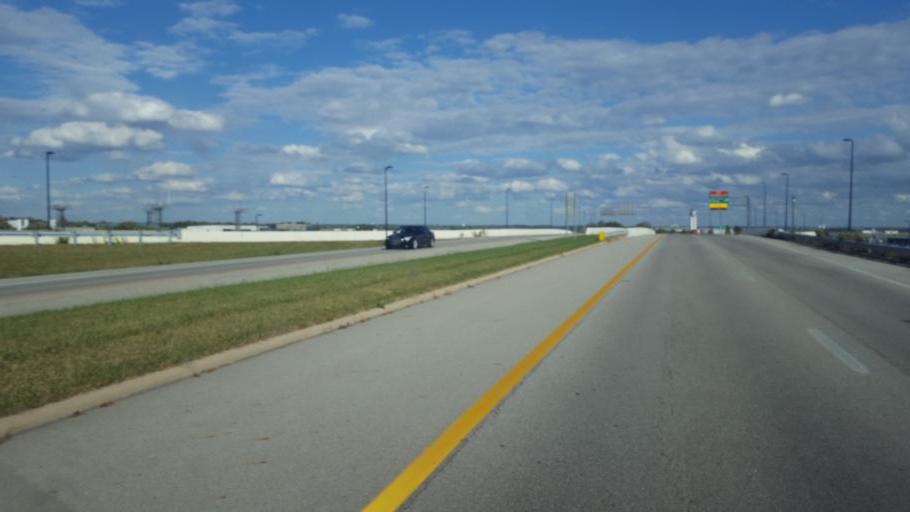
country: US
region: Ohio
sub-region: Franklin County
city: Bexley
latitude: 39.9996
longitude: -82.9145
